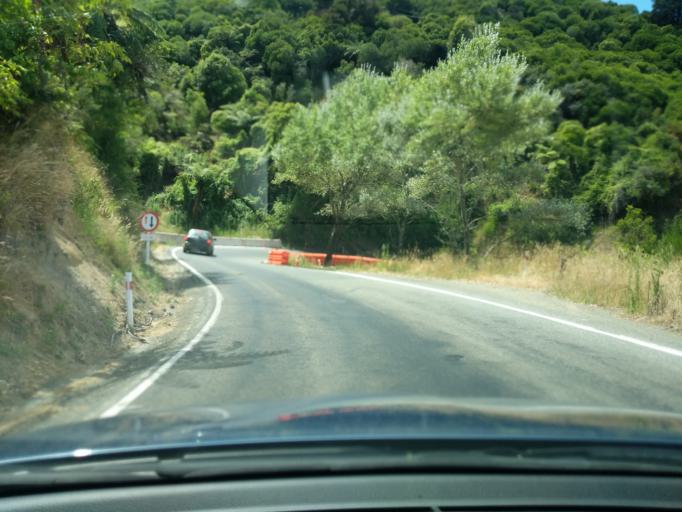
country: NZ
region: Tasman
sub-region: Tasman District
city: Motueka
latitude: -41.0489
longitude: 172.9605
